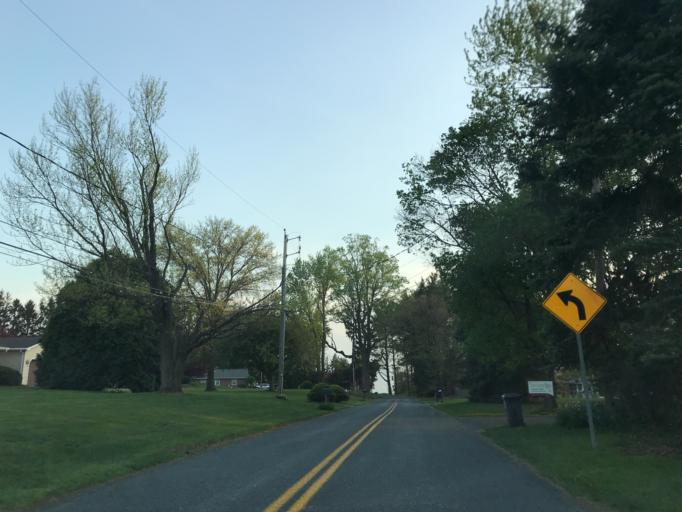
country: US
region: Maryland
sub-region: Harford County
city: Jarrettsville
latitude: 39.5910
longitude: -76.4287
